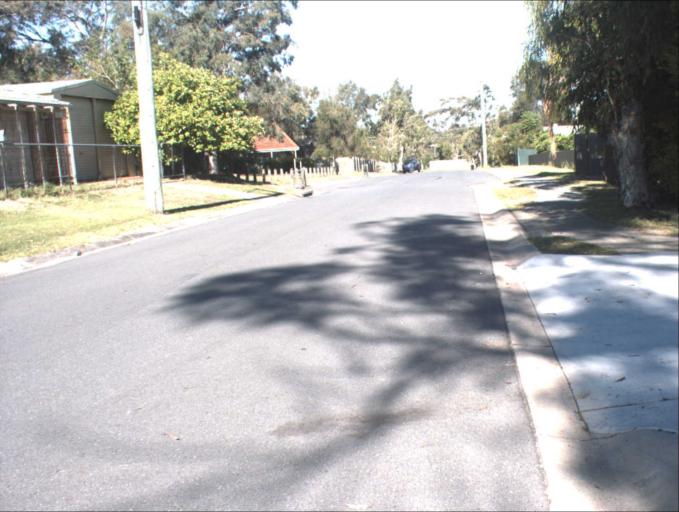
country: AU
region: Queensland
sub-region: Logan
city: Logan City
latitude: -27.6405
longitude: 153.1123
